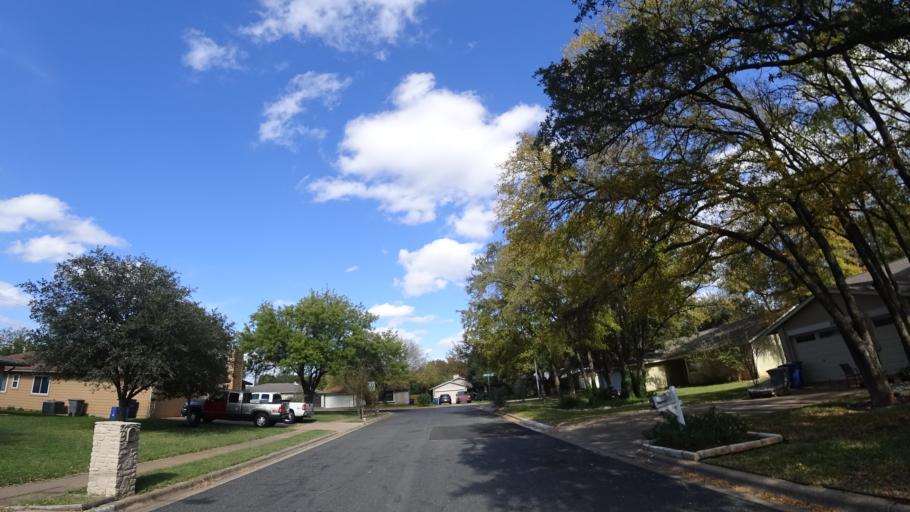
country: US
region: Texas
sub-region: Travis County
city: Wells Branch
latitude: 30.4183
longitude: -97.7170
